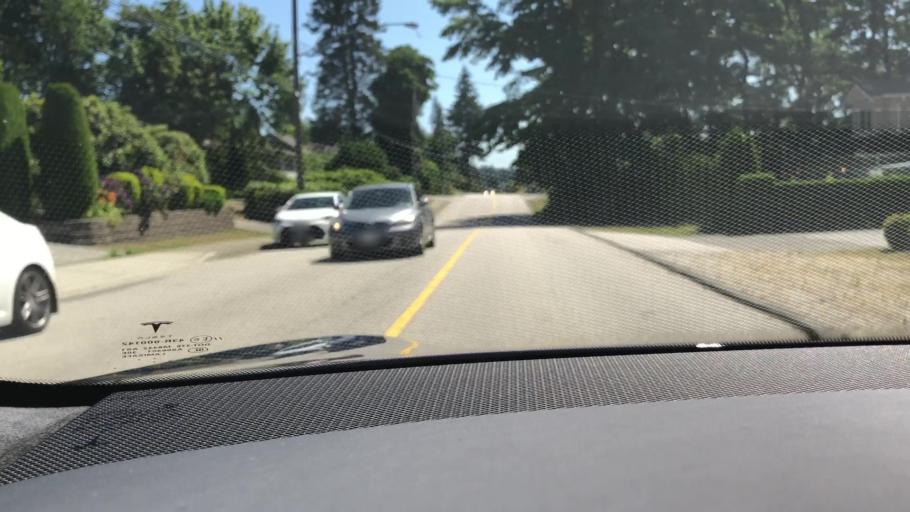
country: CA
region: British Columbia
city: Port Moody
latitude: 49.2454
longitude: -122.8691
